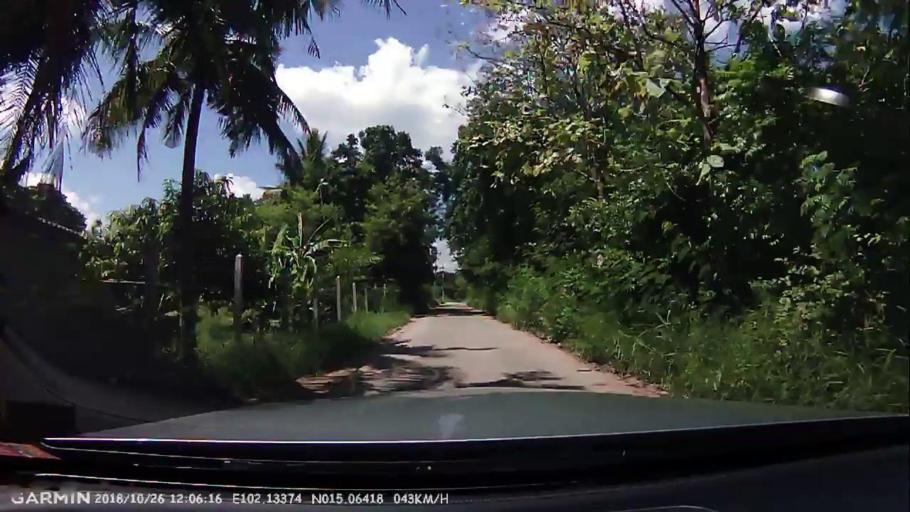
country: TH
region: Nakhon Ratchasima
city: Nakhon Ratchasima
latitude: 15.0642
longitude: 102.1336
